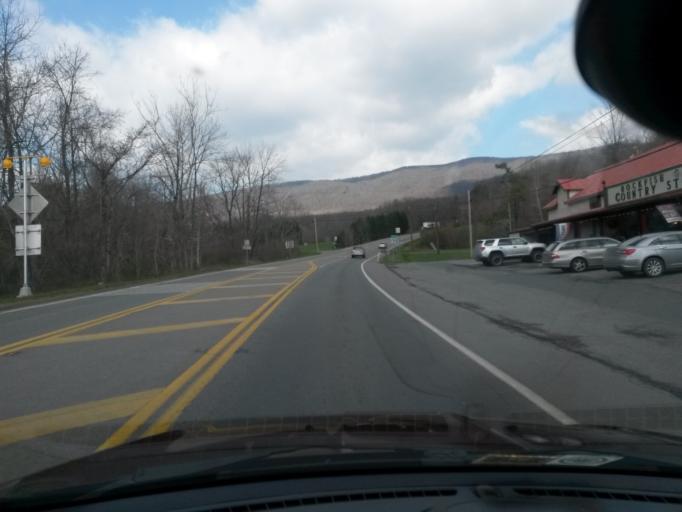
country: US
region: Virginia
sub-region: City of Waynesboro
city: Waynesboro
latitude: 38.0304
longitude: -78.8084
